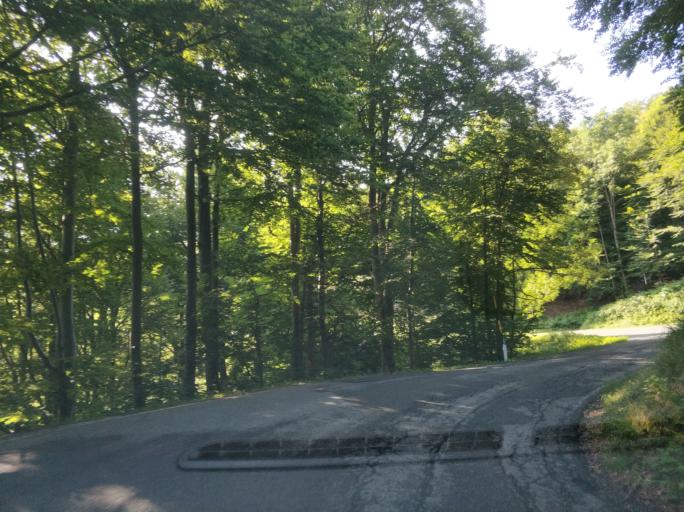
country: IT
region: Piedmont
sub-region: Provincia di Torino
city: Viu
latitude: 45.2090
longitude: 7.3748
